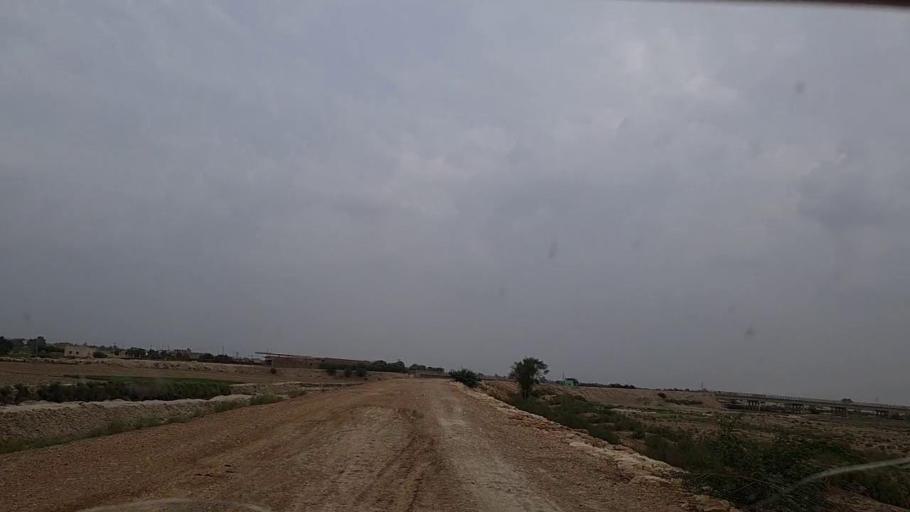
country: PK
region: Sindh
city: Johi
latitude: 26.7003
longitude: 67.5985
